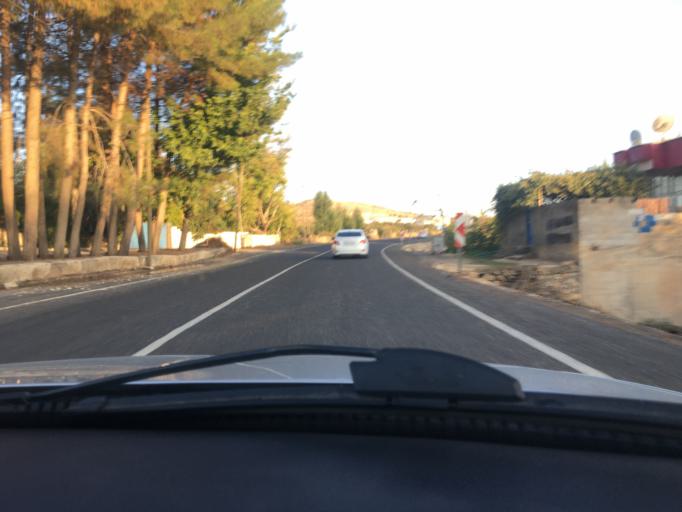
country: TR
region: Sanliurfa
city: Halfeti
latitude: 37.2086
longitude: 37.9671
